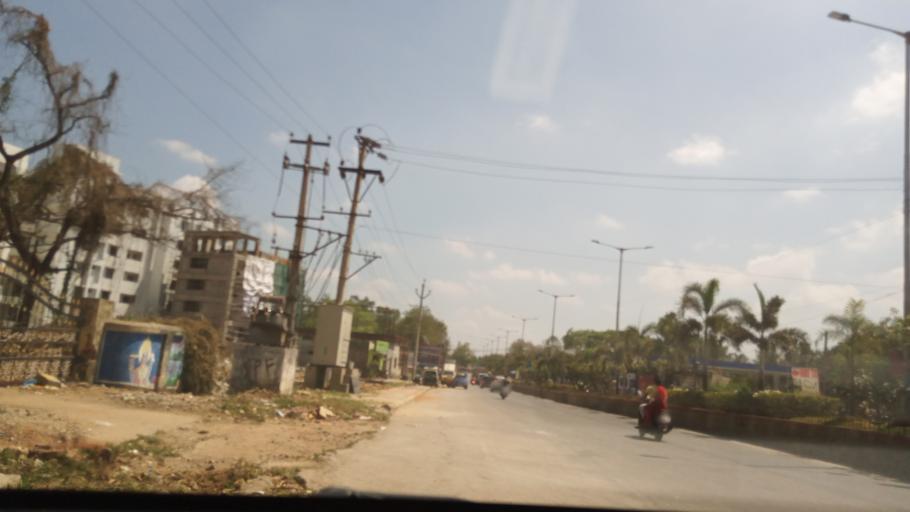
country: IN
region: Andhra Pradesh
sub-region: Chittoor
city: Akkarampalle
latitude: 13.6449
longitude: 79.4377
